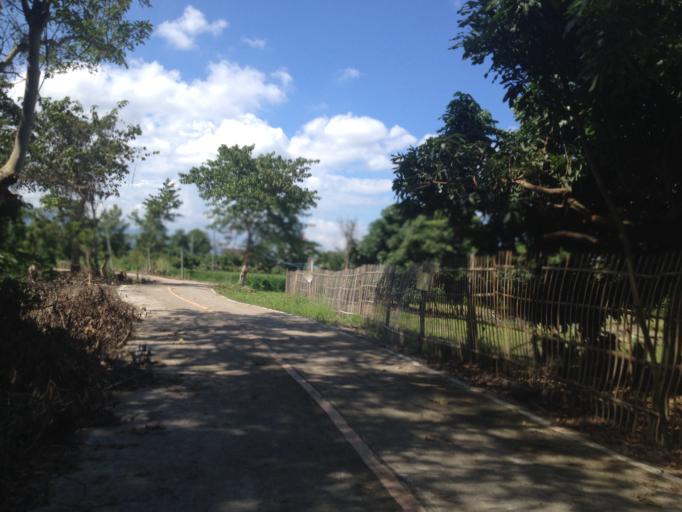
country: TH
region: Chiang Mai
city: Saraphi
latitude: 18.6990
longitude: 98.9801
